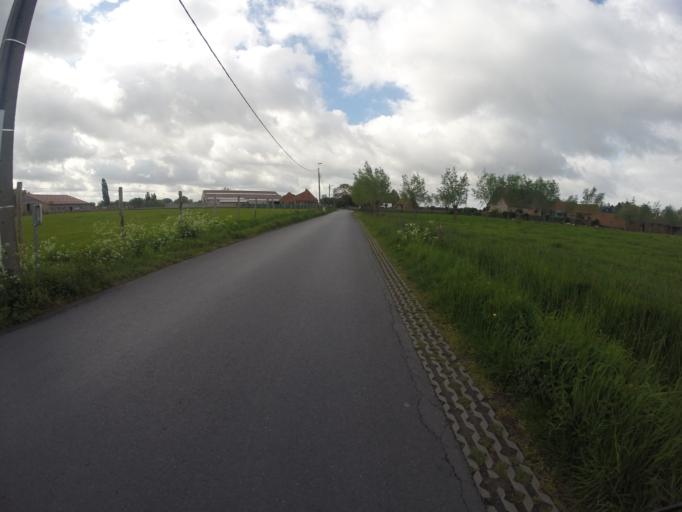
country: BE
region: Flanders
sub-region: Provincie West-Vlaanderen
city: Ruiselede
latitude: 51.0641
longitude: 3.3866
